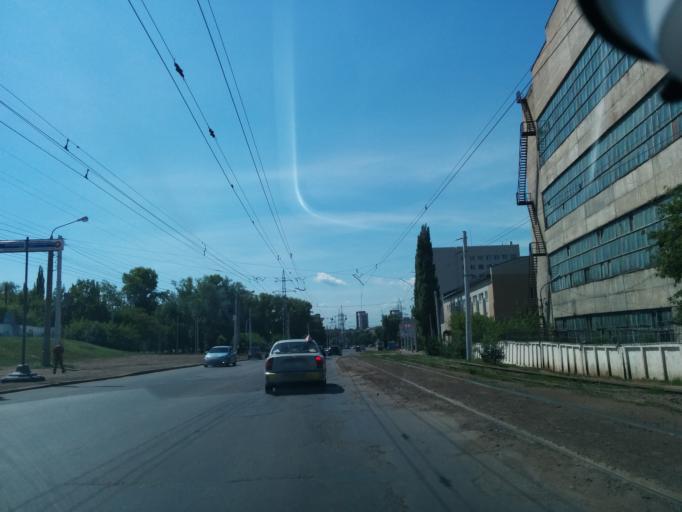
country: RU
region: Bashkortostan
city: Ufa
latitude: 54.7414
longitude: 55.9749
